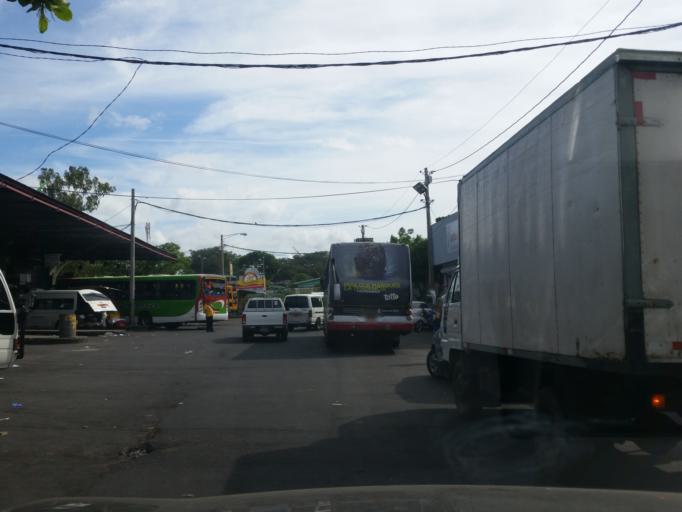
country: NI
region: Managua
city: Managua
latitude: 12.1239
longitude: -86.2444
